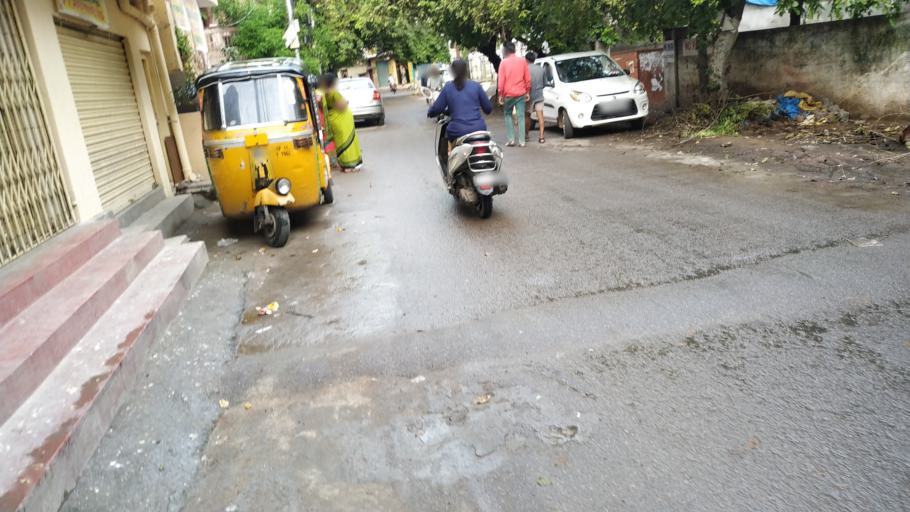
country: IN
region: Telangana
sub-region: Hyderabad
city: Malkajgiri
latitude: 17.4235
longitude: 78.5151
